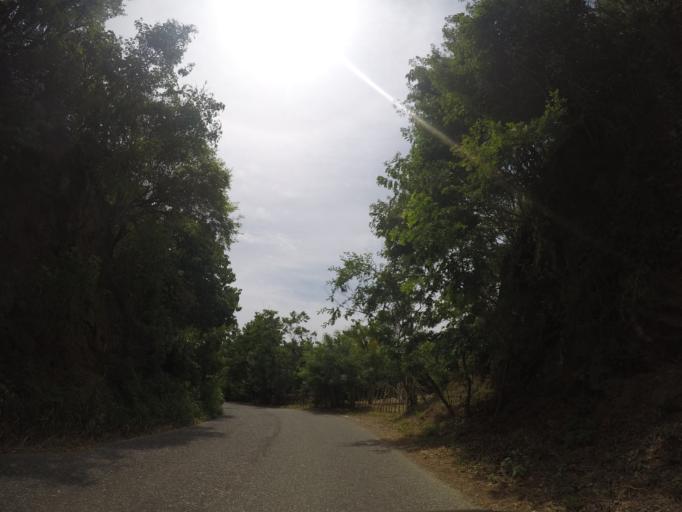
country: MX
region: Oaxaca
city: Santa Maria Tonameca
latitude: 15.6666
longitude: -96.5284
